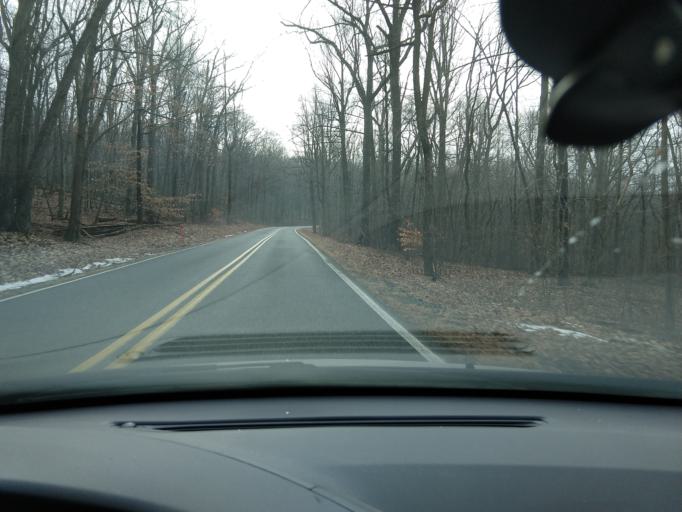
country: US
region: Pennsylvania
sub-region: Berks County
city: Birdsboro
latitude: 40.2238
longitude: -75.7737
